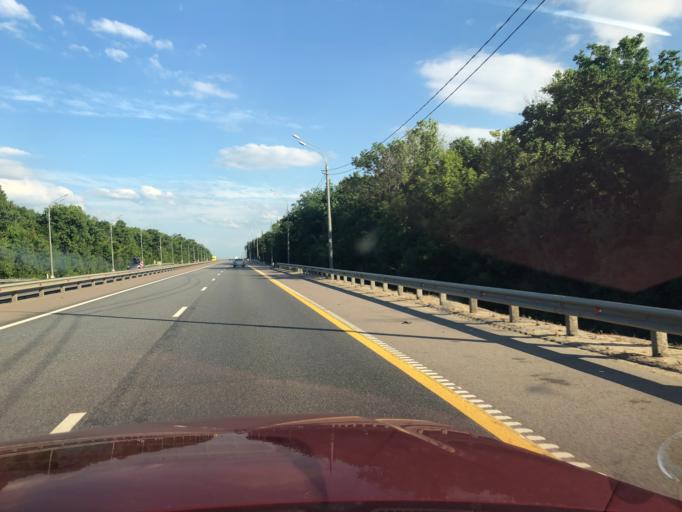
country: RU
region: Lipetsk
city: Zadonsk
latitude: 52.4180
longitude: 38.8396
